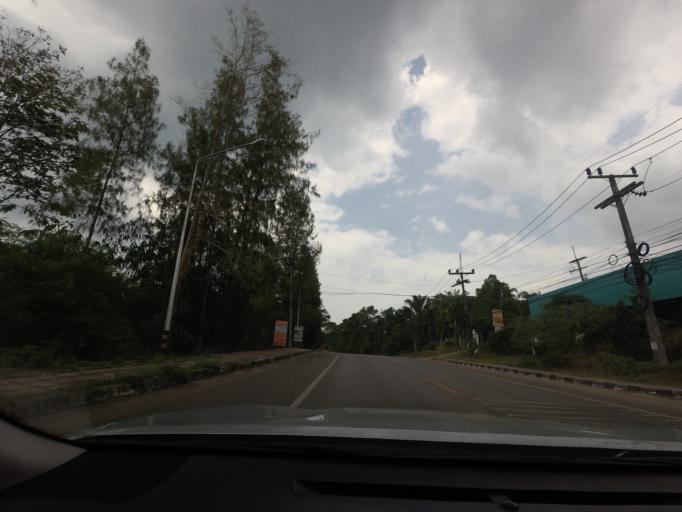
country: TH
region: Phangnga
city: Ban Ao Nang
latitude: 8.0542
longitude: 98.7565
